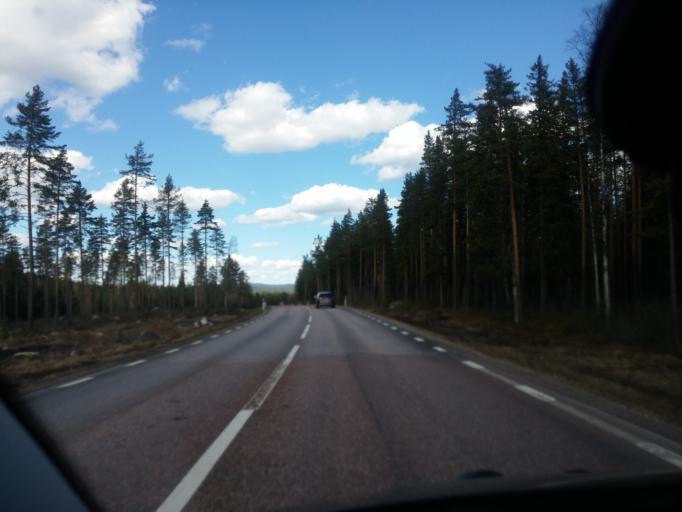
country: SE
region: Dalarna
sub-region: Faluns Kommun
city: Svardsjo
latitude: 60.7796
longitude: 15.7530
